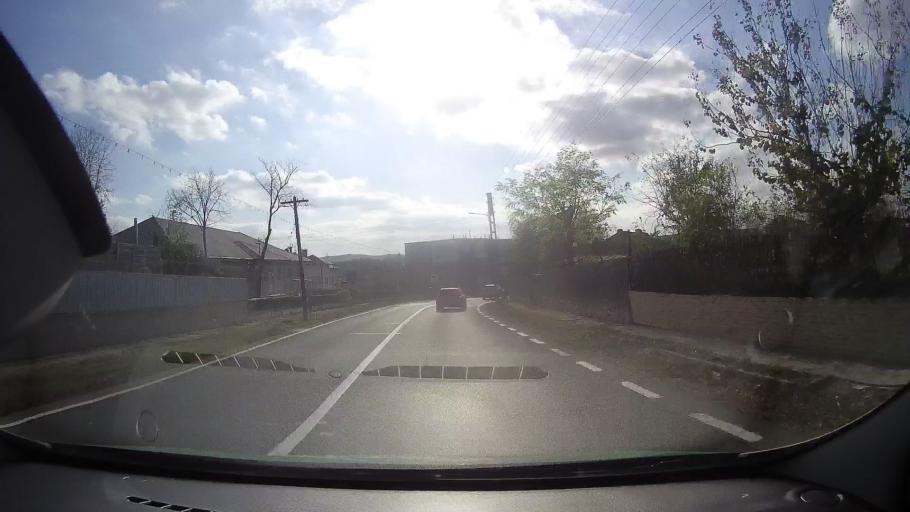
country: RO
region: Tulcea
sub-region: Comuna Nalbant
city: Nalbant
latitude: 45.0496
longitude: 28.6161
